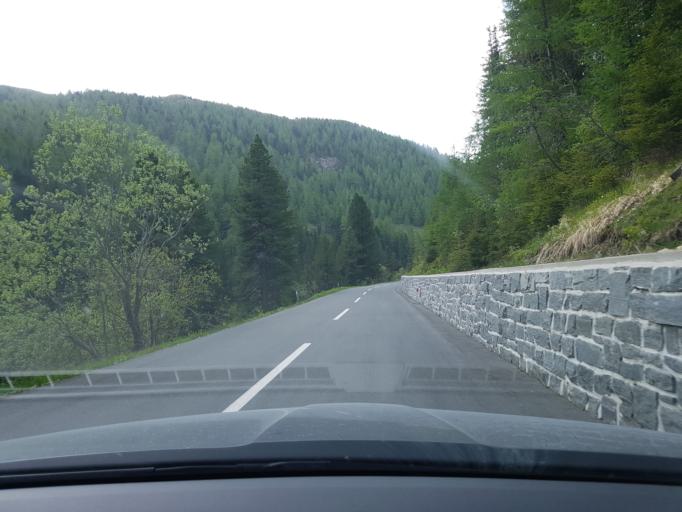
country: AT
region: Salzburg
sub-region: Politischer Bezirk Tamsweg
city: Thomatal
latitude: 46.9505
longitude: 13.7322
